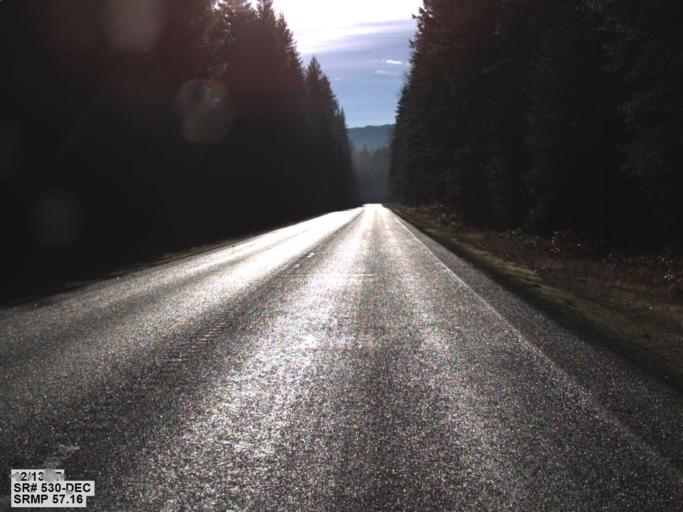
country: US
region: Washington
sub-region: Snohomish County
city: Darrington
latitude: 48.3529
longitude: -121.5399
